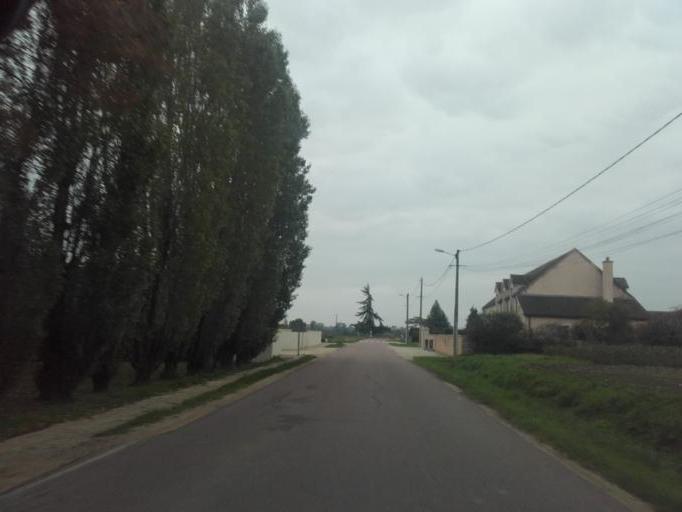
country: FR
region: Bourgogne
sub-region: Departement de Saone-et-Loire
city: Demigny
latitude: 46.9567
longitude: 4.8566
